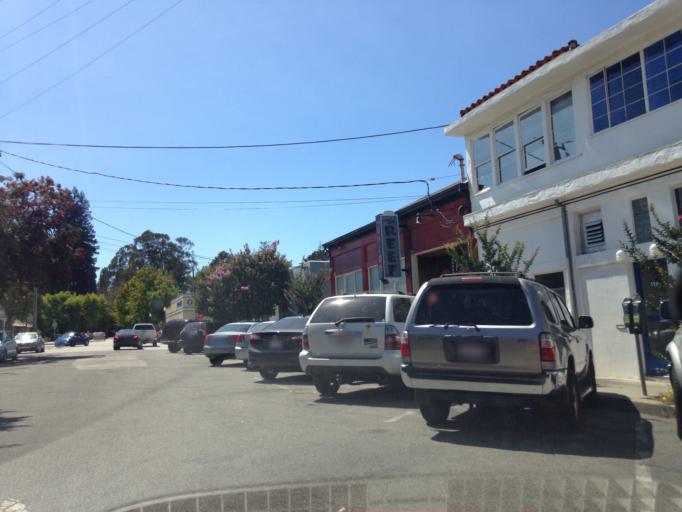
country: US
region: California
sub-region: Santa Cruz County
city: Santa Cruz
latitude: 36.9757
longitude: -122.0281
